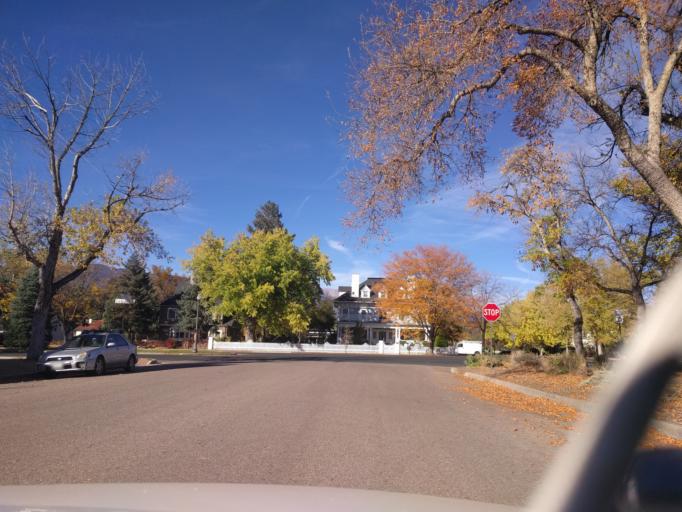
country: US
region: Colorado
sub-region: El Paso County
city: Colorado Springs
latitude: 38.8521
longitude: -104.8238
